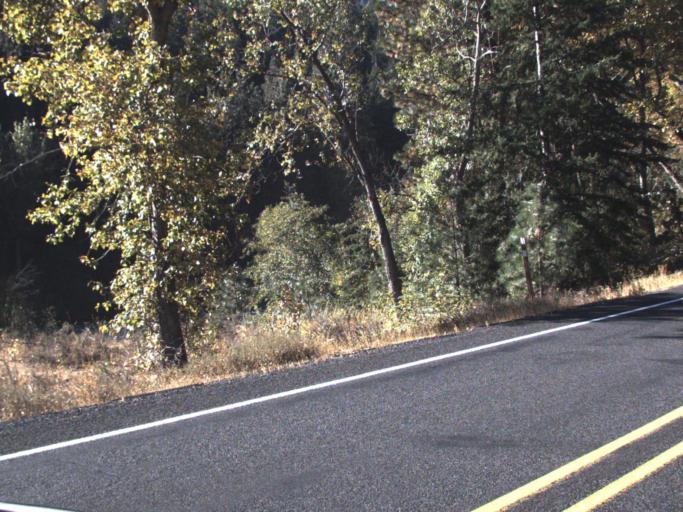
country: US
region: Washington
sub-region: Yakima County
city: Tieton
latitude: 46.6944
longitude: -120.9025
